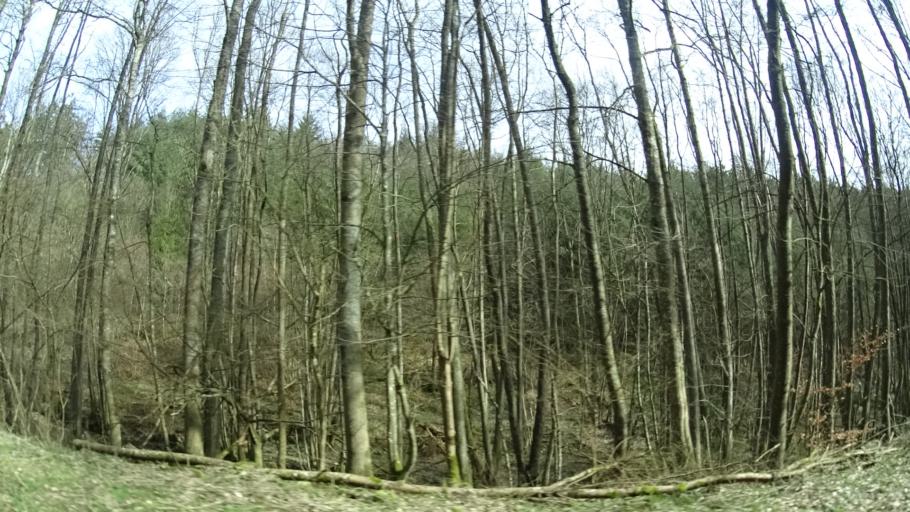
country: DE
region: Rheinland-Pfalz
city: Munchwald
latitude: 49.9099
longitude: 7.6699
